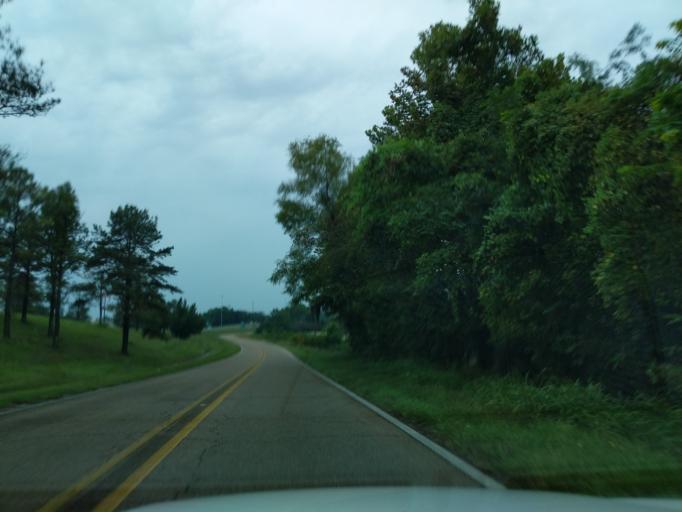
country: US
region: Mississippi
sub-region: Warren County
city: Vicksburg
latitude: 32.3206
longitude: -90.8789
